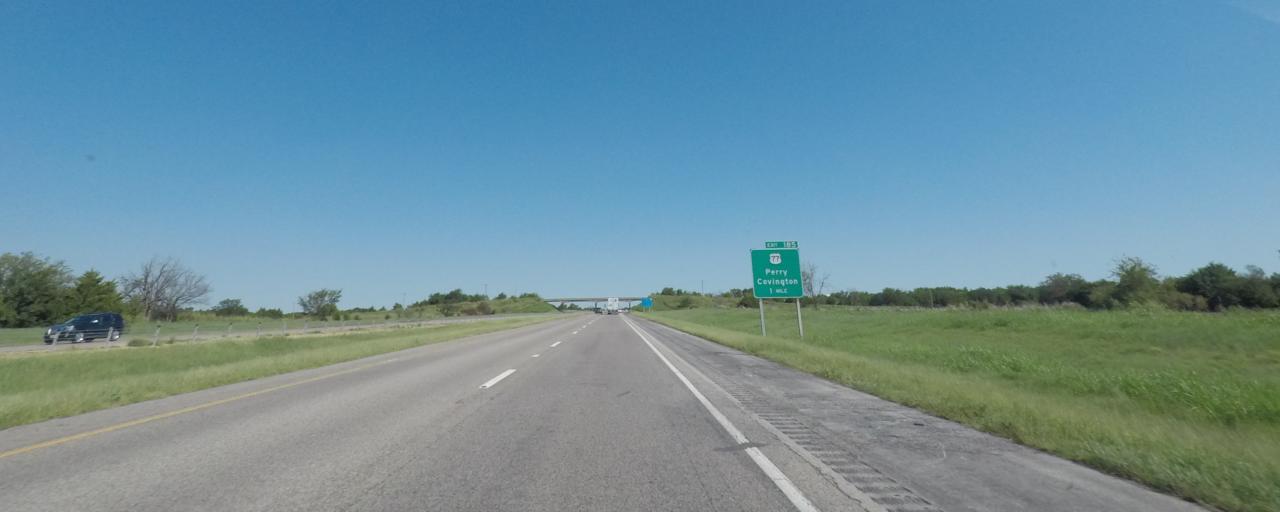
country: US
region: Oklahoma
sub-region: Noble County
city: Perry
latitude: 36.2574
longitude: -97.3258
